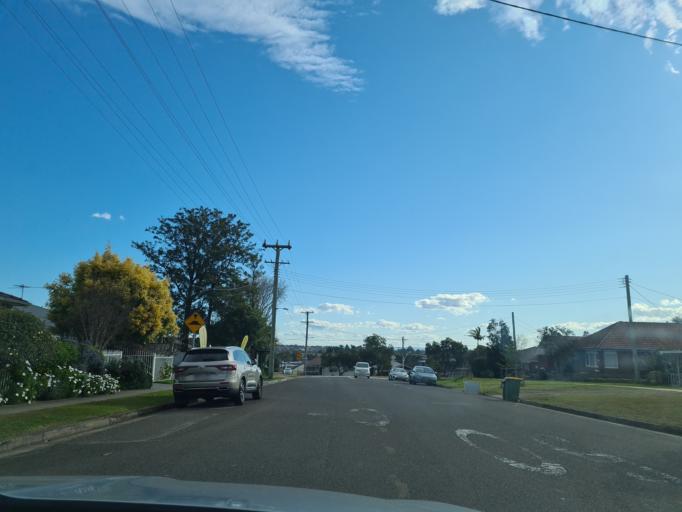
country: AU
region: New South Wales
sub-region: Parramatta
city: City of Parramatta
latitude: -33.7938
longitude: 151.0056
